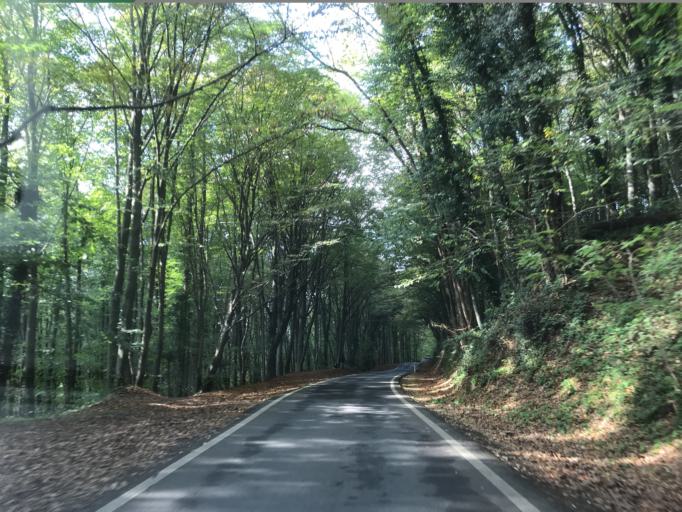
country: TR
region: Istanbul
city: Arikoey
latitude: 41.1872
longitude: 28.9850
